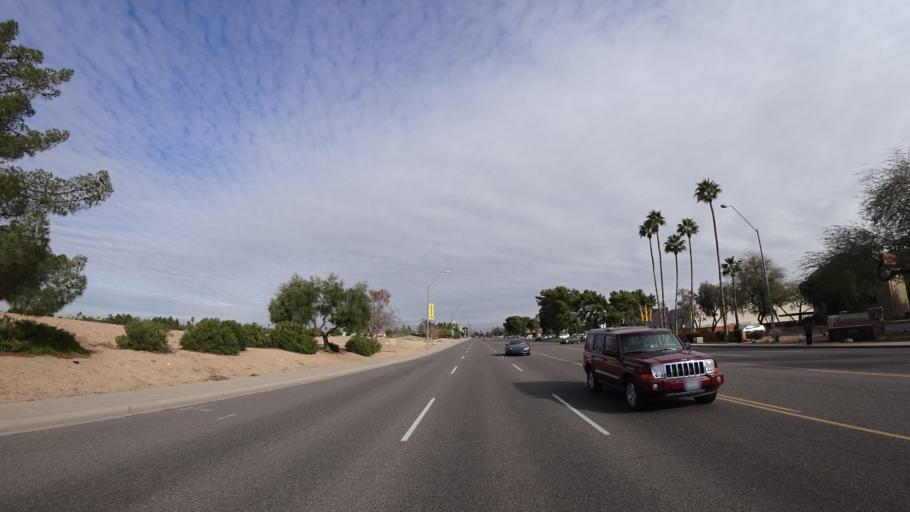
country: US
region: Arizona
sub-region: Maricopa County
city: Glendale
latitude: 33.6078
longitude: -112.1514
